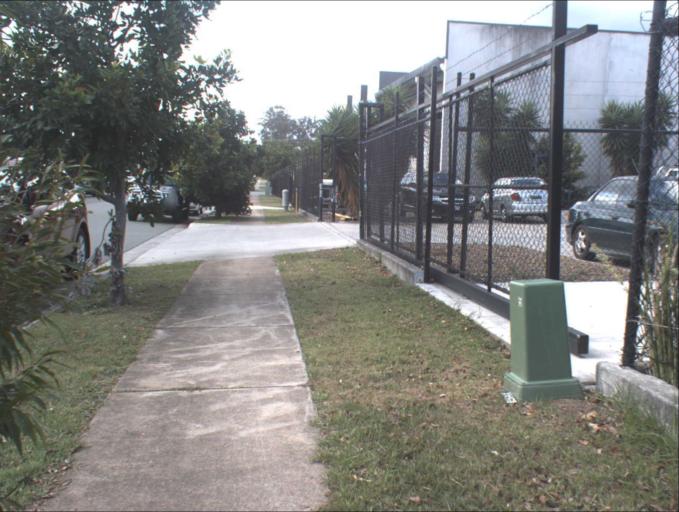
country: AU
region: Queensland
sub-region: Logan
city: Slacks Creek
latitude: -27.6638
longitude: 153.1332
